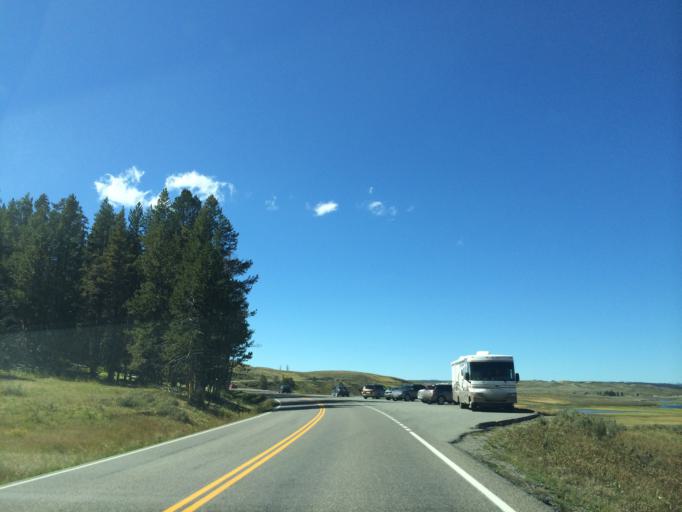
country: US
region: Montana
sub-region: Gallatin County
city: West Yellowstone
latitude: 44.6301
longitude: -110.4385
